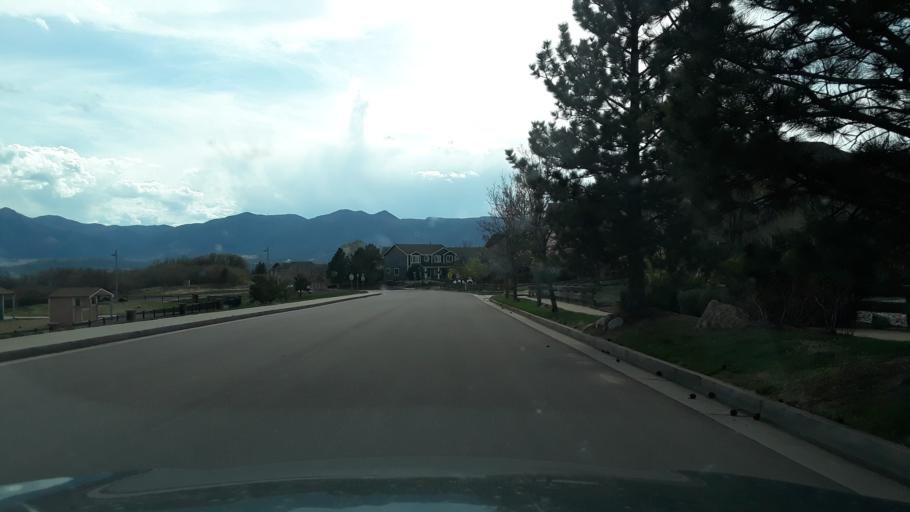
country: US
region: Colorado
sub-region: El Paso County
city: Gleneagle
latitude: 39.0131
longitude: -104.8036
